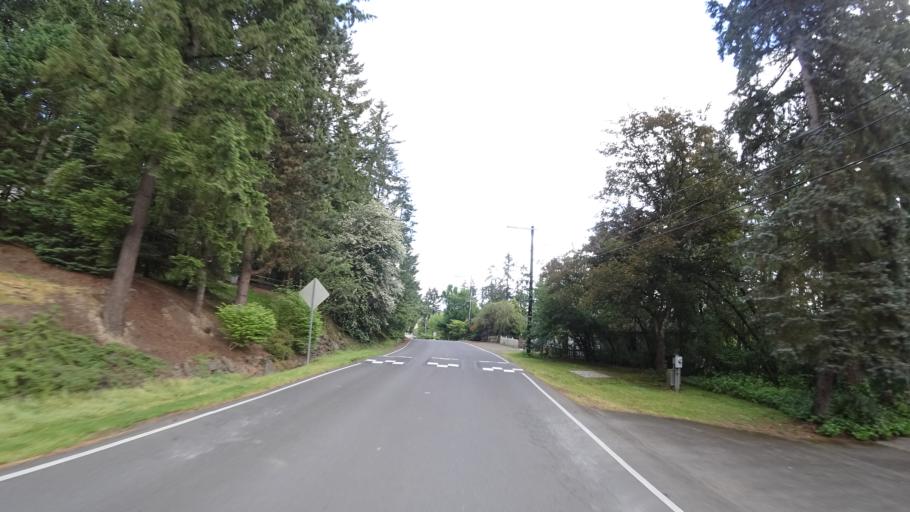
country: US
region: Oregon
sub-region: Washington County
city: Beaverton
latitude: 45.4722
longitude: -122.8375
